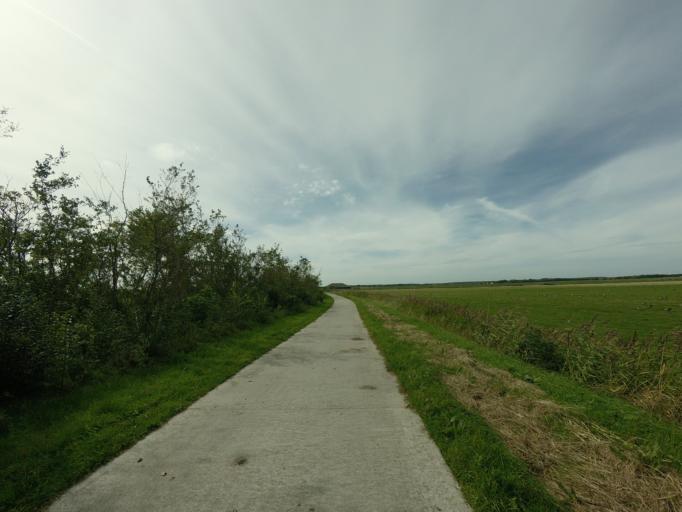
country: NL
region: North Holland
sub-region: Gemeente Texel
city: Den Burg
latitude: 53.0743
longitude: 4.8057
